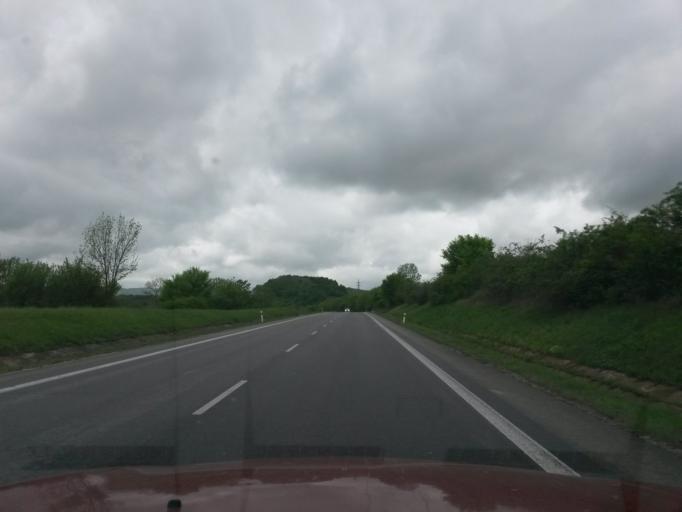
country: SK
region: Kosicky
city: Medzev
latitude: 48.6097
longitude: 20.8536
